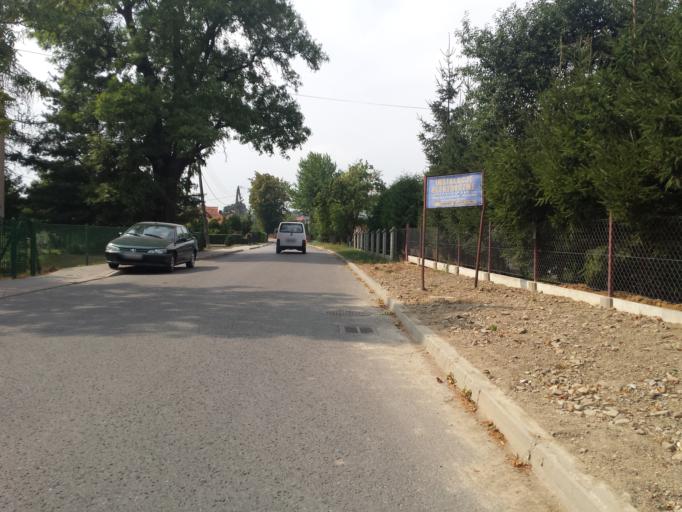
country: PL
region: Subcarpathian Voivodeship
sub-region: Powiat rzeszowski
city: Dynow
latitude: 49.8184
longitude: 22.2258
